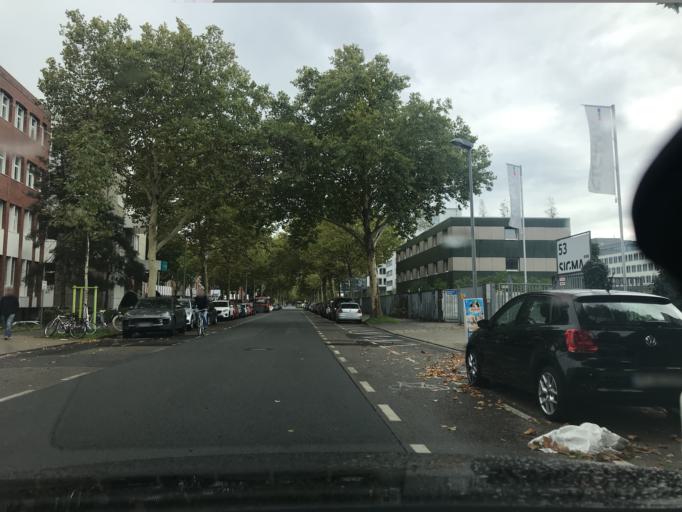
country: DE
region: North Rhine-Westphalia
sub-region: Regierungsbezirk Dusseldorf
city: Meerbusch
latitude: 51.2415
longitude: 6.7215
